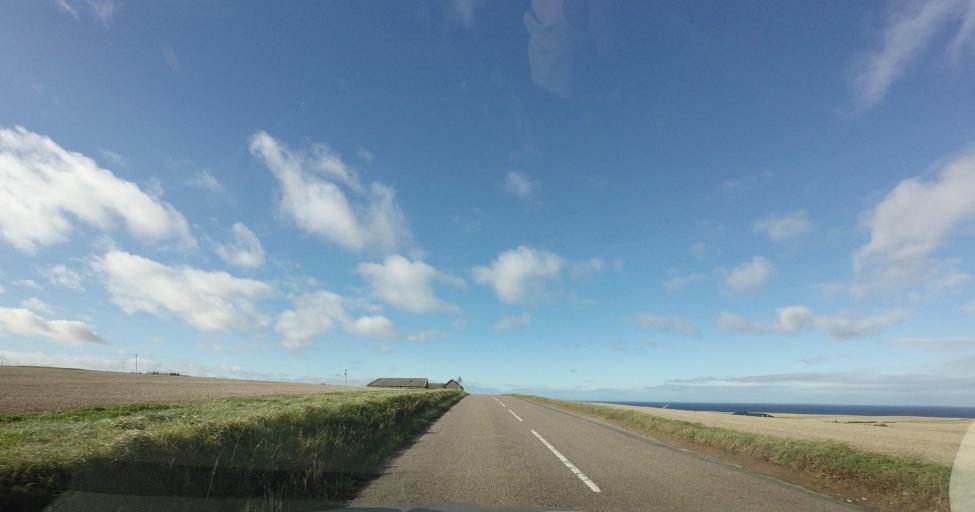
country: GB
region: Scotland
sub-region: Aberdeenshire
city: Macduff
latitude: 57.6633
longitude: -2.4202
